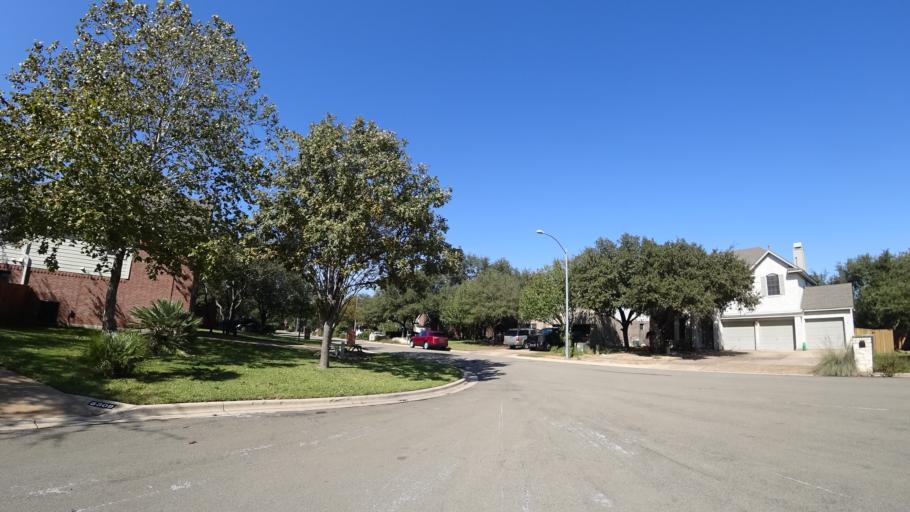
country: US
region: Texas
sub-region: Travis County
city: Shady Hollow
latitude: 30.2045
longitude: -97.8672
